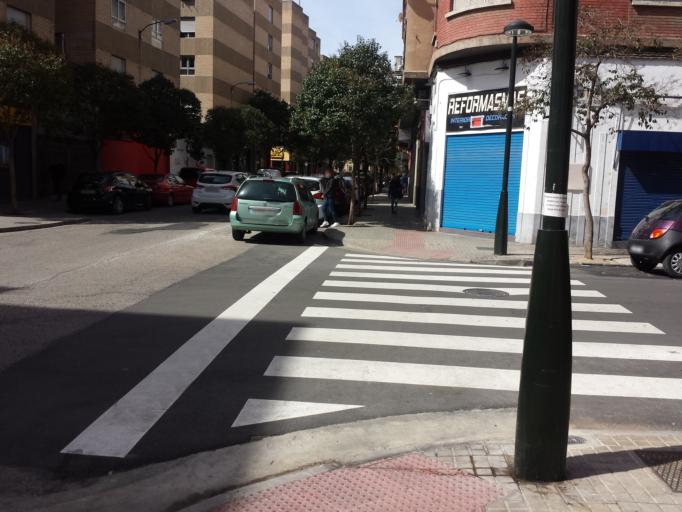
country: ES
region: Aragon
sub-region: Provincia de Zaragoza
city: Zaragoza
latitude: 41.6449
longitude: -0.8664
